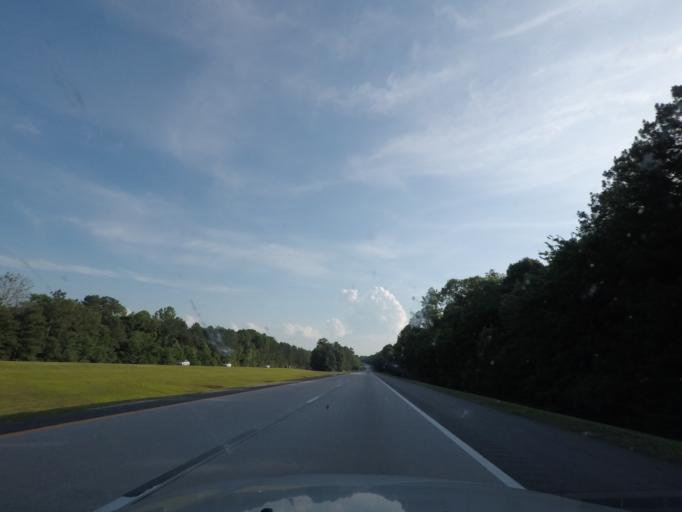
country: US
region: North Carolina
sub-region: Granville County
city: Creedmoor
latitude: 36.1873
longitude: -78.6905
